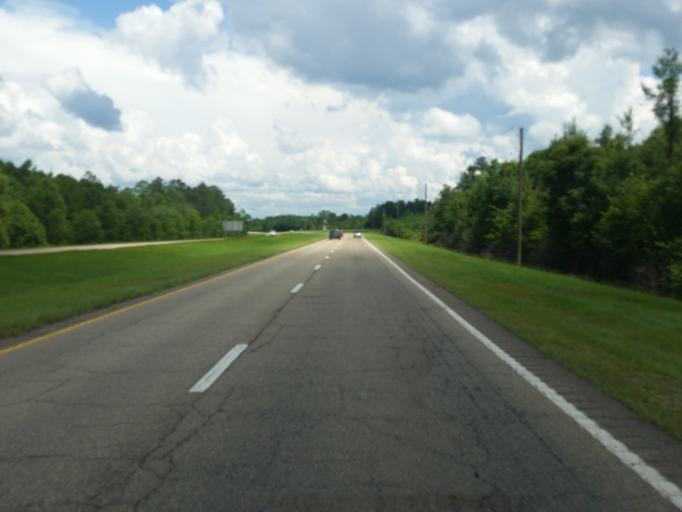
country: US
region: Mississippi
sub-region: Perry County
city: New Augusta
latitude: 31.1475
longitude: -88.8850
